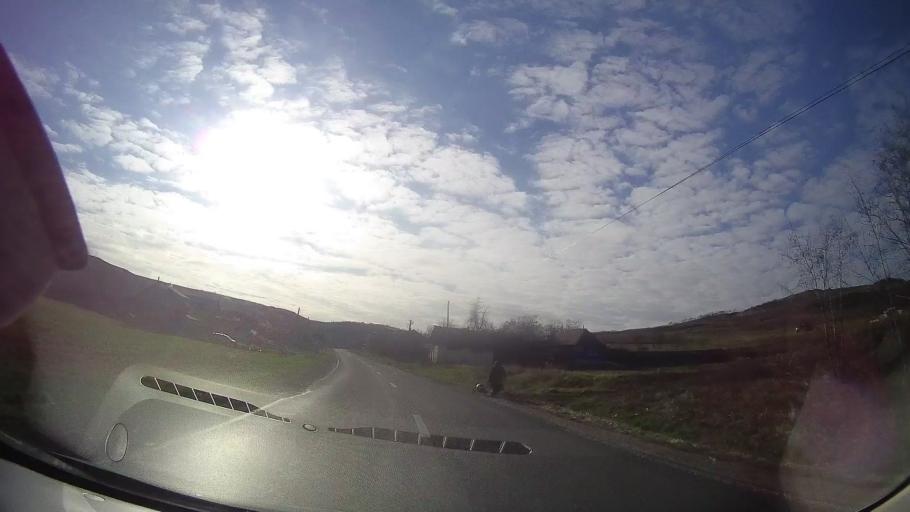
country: RO
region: Cluj
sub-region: Comuna Cojocna
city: Cojocna
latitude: 46.8090
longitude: 23.8496
